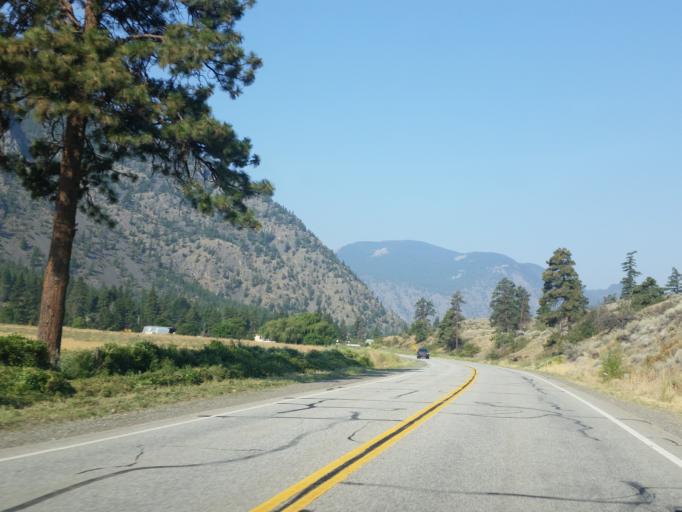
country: CA
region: British Columbia
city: Oliver
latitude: 49.2182
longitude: -119.9224
